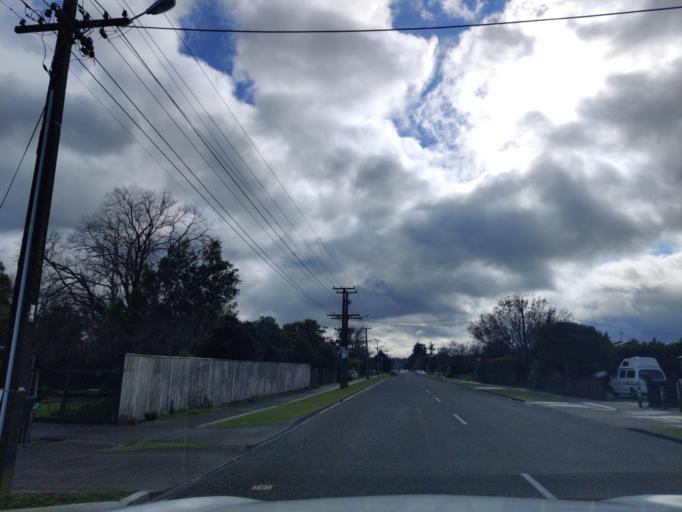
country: NZ
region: Manawatu-Wanganui
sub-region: Palmerston North City
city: Palmerston North
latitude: -40.2817
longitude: 175.7564
